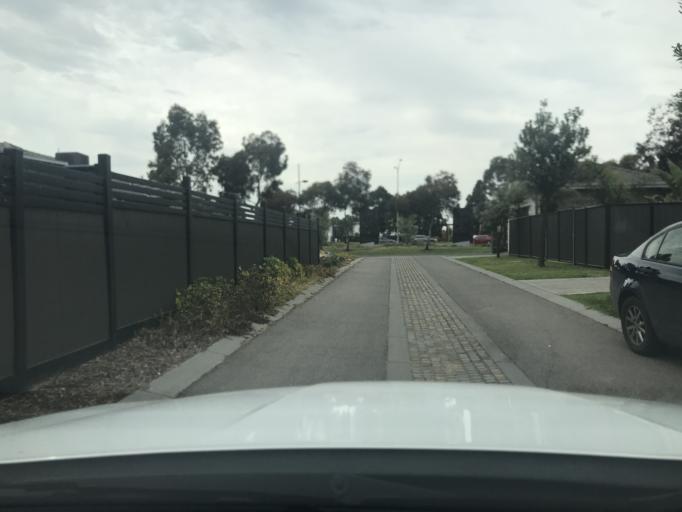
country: AU
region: Victoria
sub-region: Hume
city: Roxburgh Park
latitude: -37.5938
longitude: 144.9044
